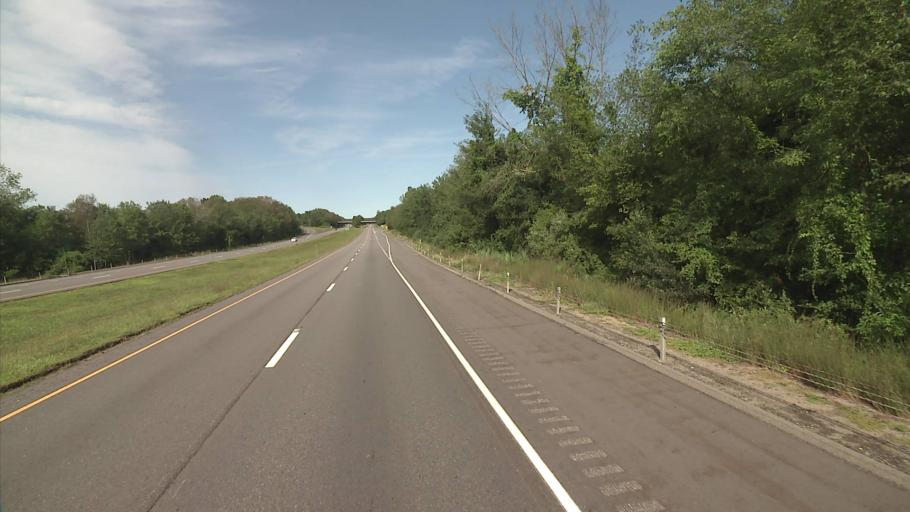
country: US
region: Connecticut
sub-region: New London County
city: Montville Center
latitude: 41.5713
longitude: -72.2006
